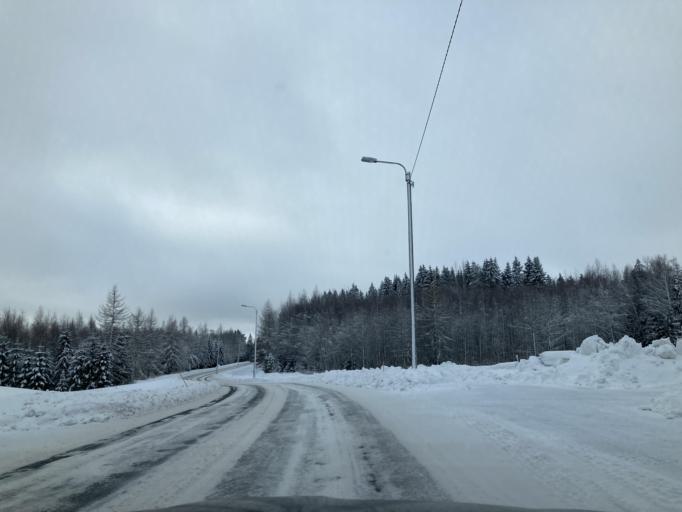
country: FI
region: Central Finland
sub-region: Jaemsae
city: Jaemsae
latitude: 61.8646
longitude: 25.2390
